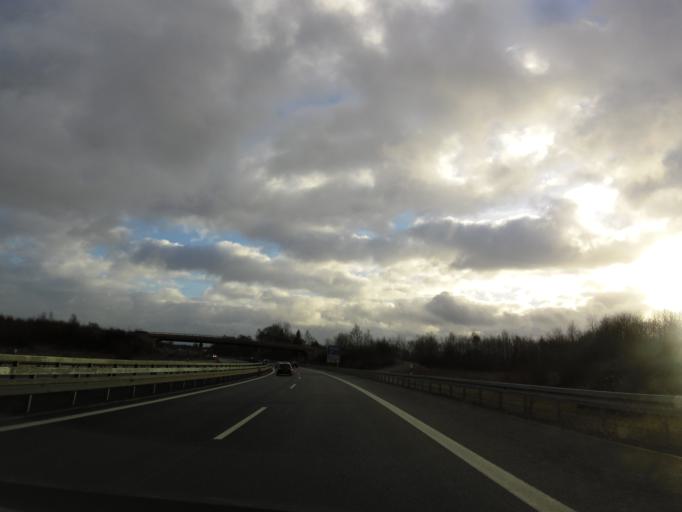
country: DE
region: Bavaria
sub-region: Upper Franconia
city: Thierstein
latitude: 50.0919
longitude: 12.0992
